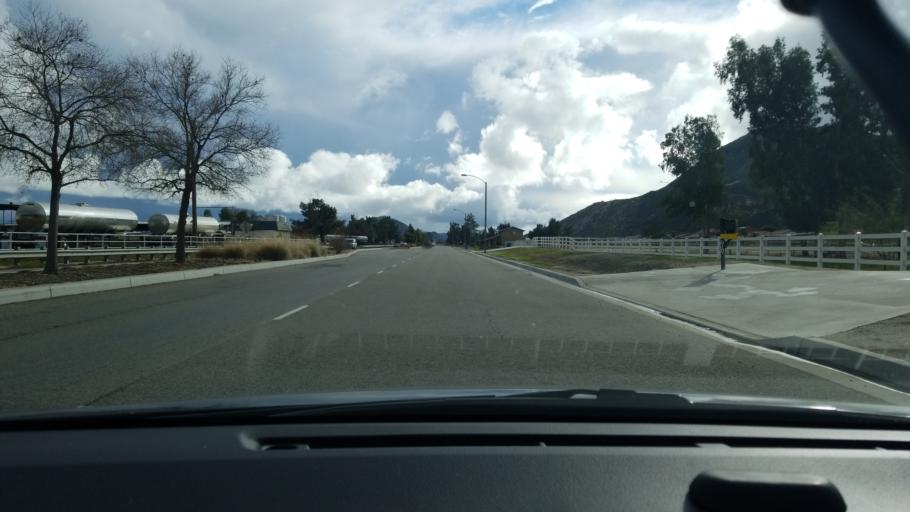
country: US
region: California
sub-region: Riverside County
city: Green Acres
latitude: 33.7972
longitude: -117.0338
